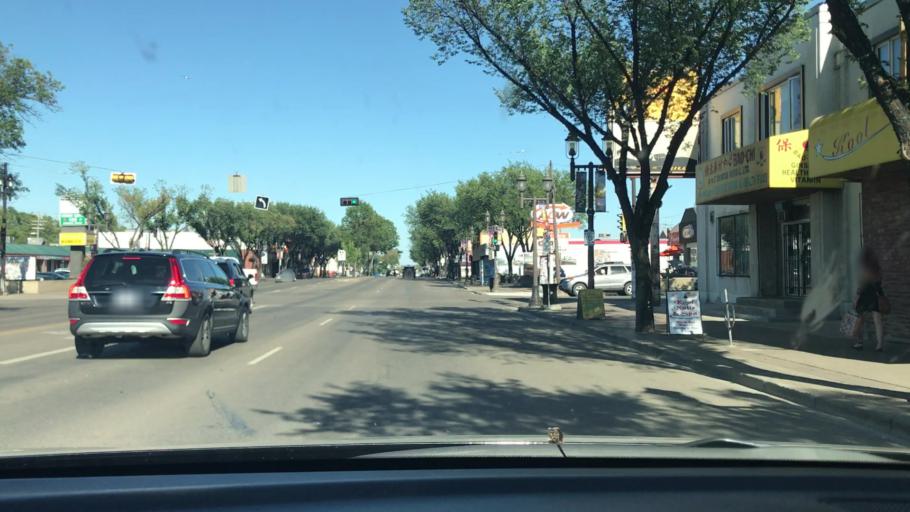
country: CA
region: Alberta
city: Edmonton
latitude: 53.5180
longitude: -113.4920
